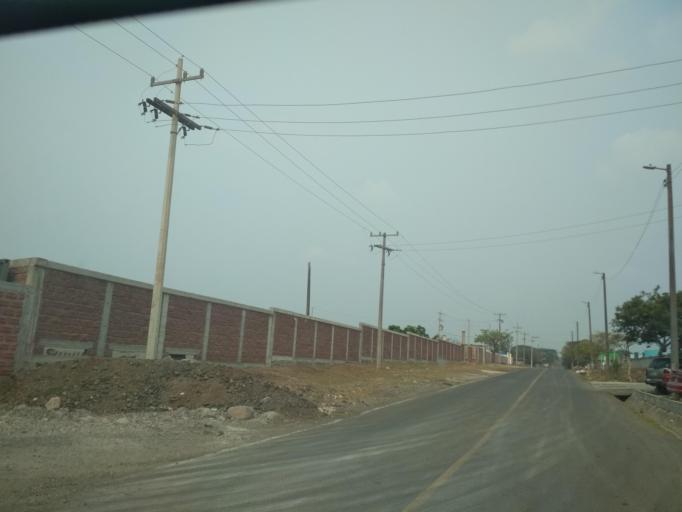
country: MX
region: Veracruz
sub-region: Veracruz
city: Delfino Victoria (Santa Fe)
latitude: 19.2101
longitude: -96.2510
